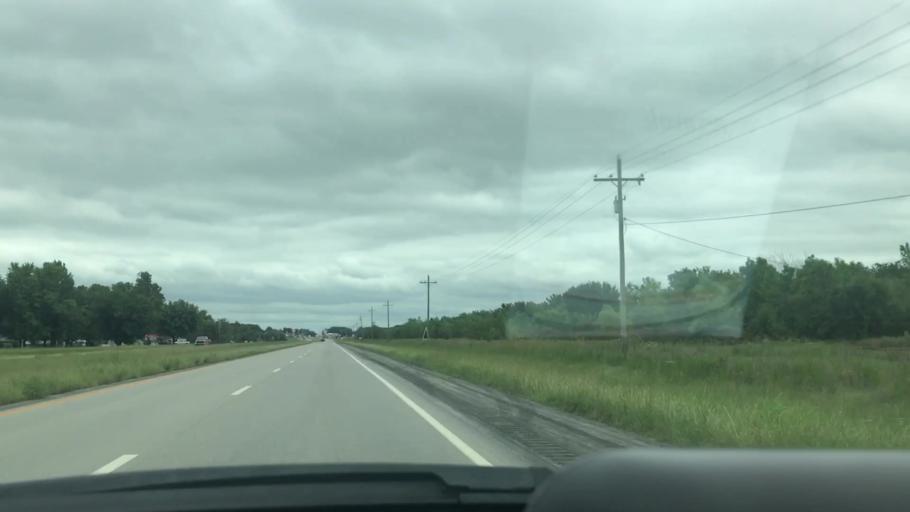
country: US
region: Oklahoma
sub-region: Mayes County
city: Pryor
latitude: 36.4239
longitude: -95.2764
